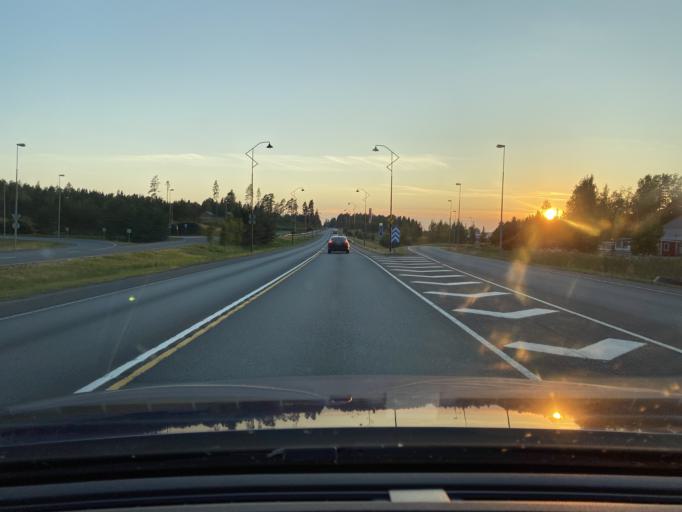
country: FI
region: Pirkanmaa
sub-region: Luoteis-Pirkanmaa
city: Ikaalinen
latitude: 61.7529
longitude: 23.0717
